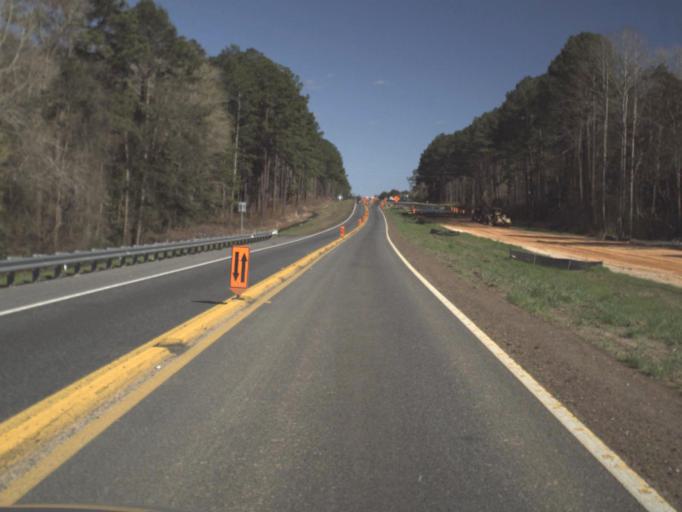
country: US
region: Florida
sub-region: Gadsden County
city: Midway
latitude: 30.5533
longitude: -84.5086
